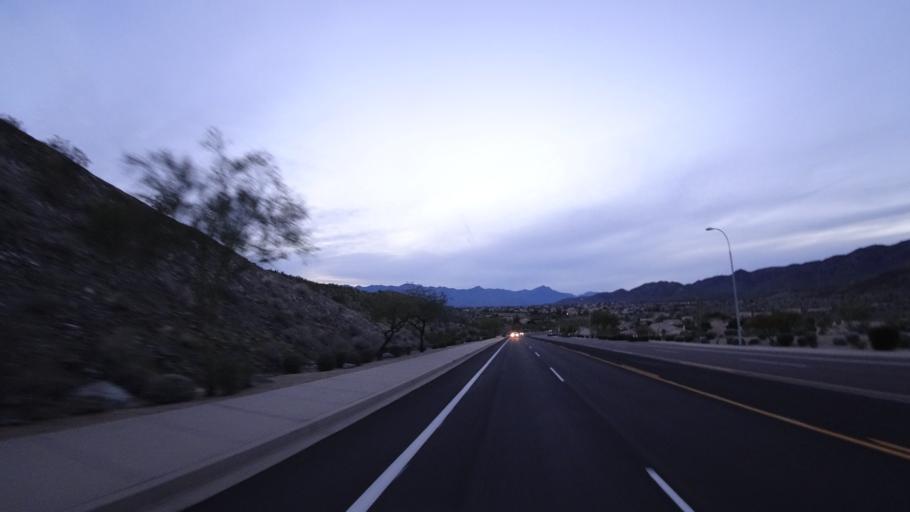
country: US
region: Arizona
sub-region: Maricopa County
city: Laveen
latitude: 33.3044
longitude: -112.0715
